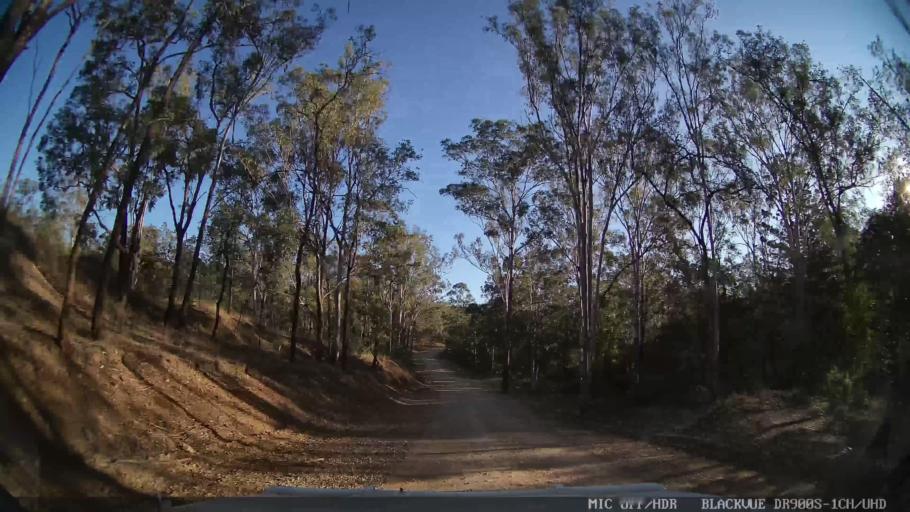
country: AU
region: Queensland
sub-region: Gladstone
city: Toolooa
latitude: -24.6835
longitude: 151.3304
